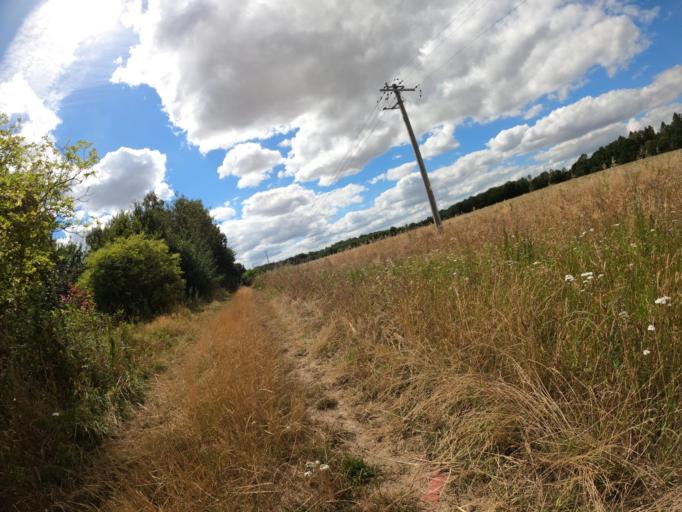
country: PL
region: West Pomeranian Voivodeship
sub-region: Powiat swidwinski
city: Swidwin
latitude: 53.7499
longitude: 15.8260
